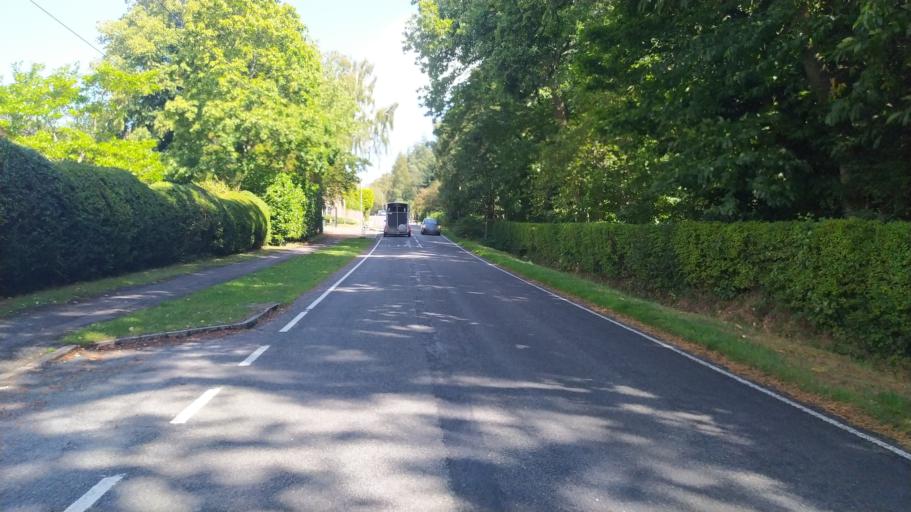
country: GB
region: England
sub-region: Hampshire
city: Liss
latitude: 51.0763
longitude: -0.8866
